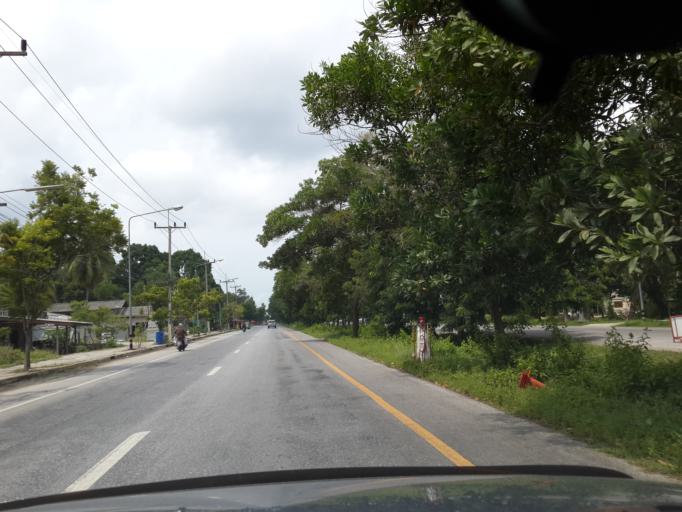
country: TH
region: Pattani
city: Yaring
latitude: 6.8620
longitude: 101.3670
